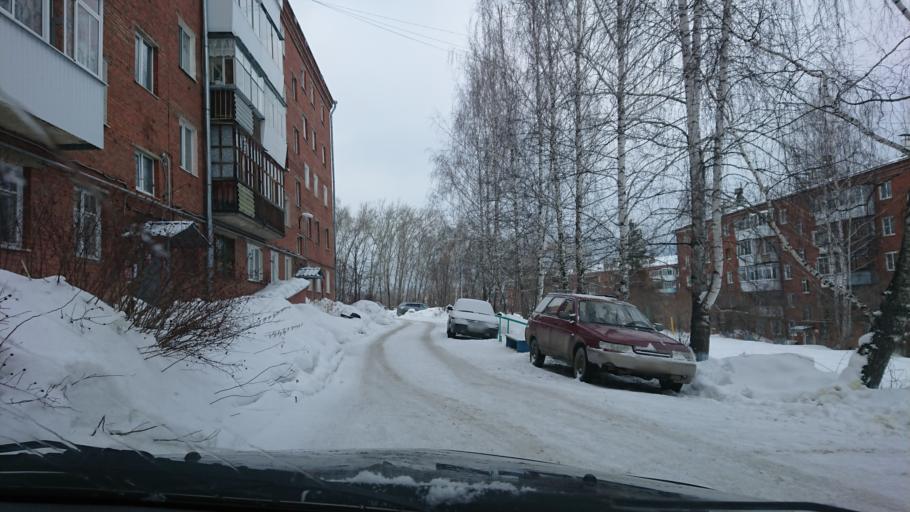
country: RU
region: Sverdlovsk
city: Degtyarsk
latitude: 56.6918
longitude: 60.0867
